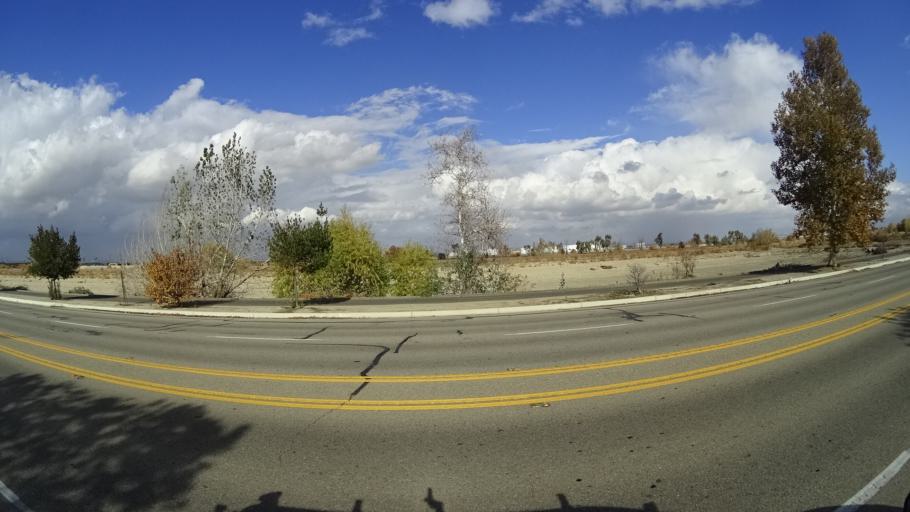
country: US
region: California
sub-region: Kern County
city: Greenacres
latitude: 35.3619
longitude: -119.0831
